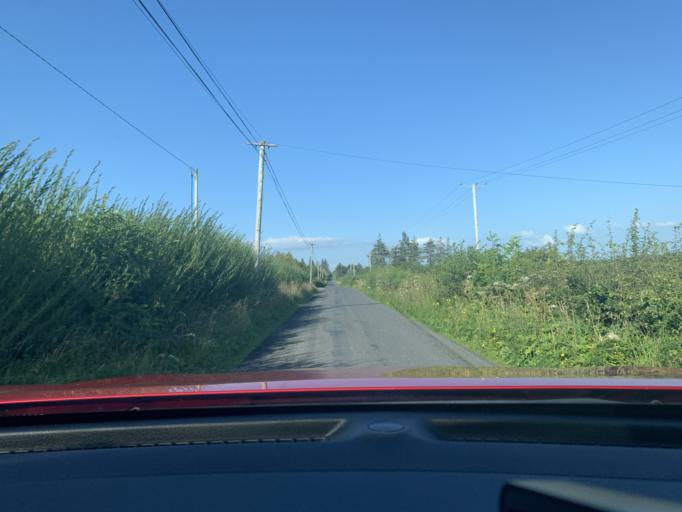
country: IE
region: Connaught
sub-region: Sligo
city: Tobercurry
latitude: 54.1145
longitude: -8.7627
